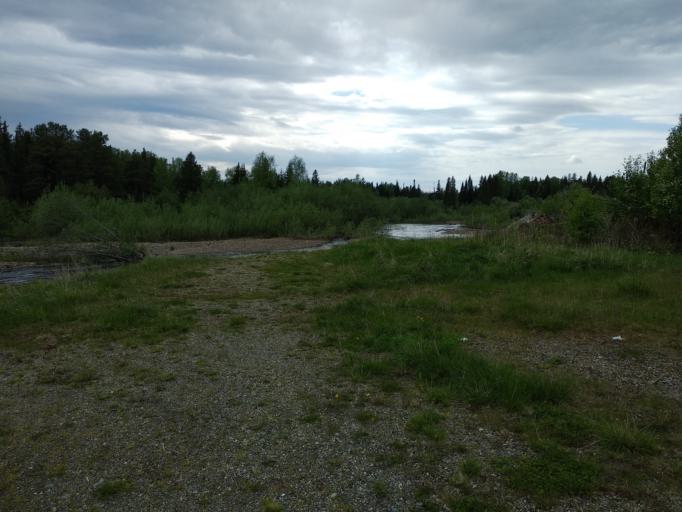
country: RU
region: Sverdlovsk
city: Karpinsk
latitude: 59.7142
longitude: 59.5983
